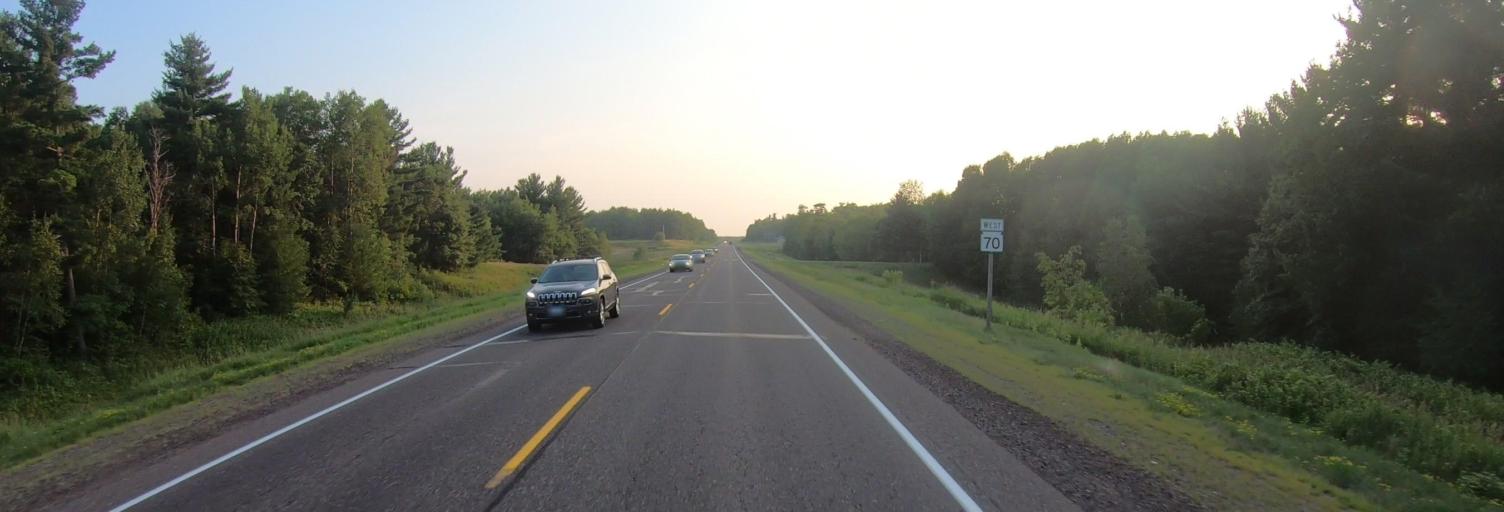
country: US
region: Wisconsin
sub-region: Burnett County
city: Siren
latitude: 45.7735
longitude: -92.4598
